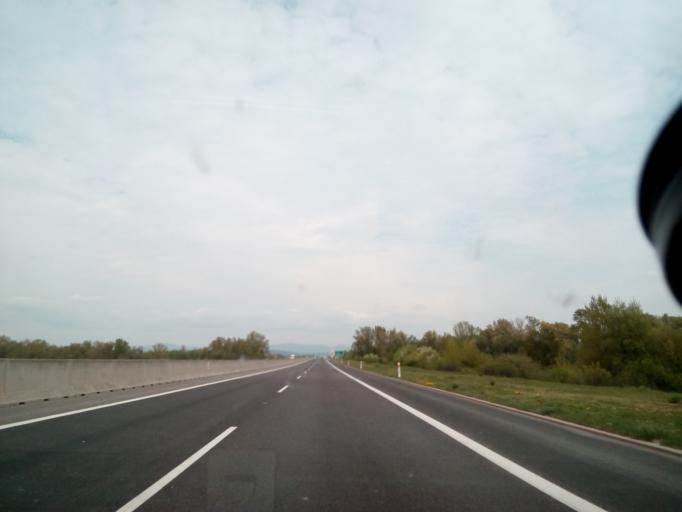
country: SK
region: Trenciansky
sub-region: Okres Nove Mesto nad Vahom
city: Nove Mesto nad Vahom
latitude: 48.6983
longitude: 17.8722
